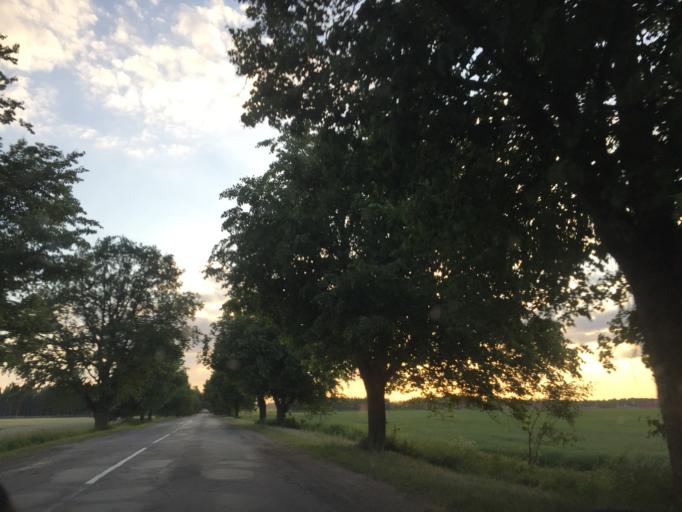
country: LV
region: Sigulda
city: Sigulda
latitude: 57.1376
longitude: 24.8914
